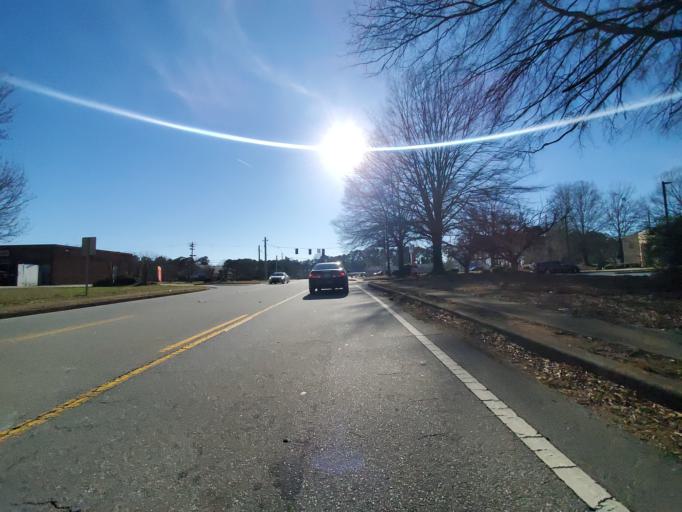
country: US
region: Georgia
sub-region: Gwinnett County
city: Snellville
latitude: 33.8888
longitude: -84.0605
